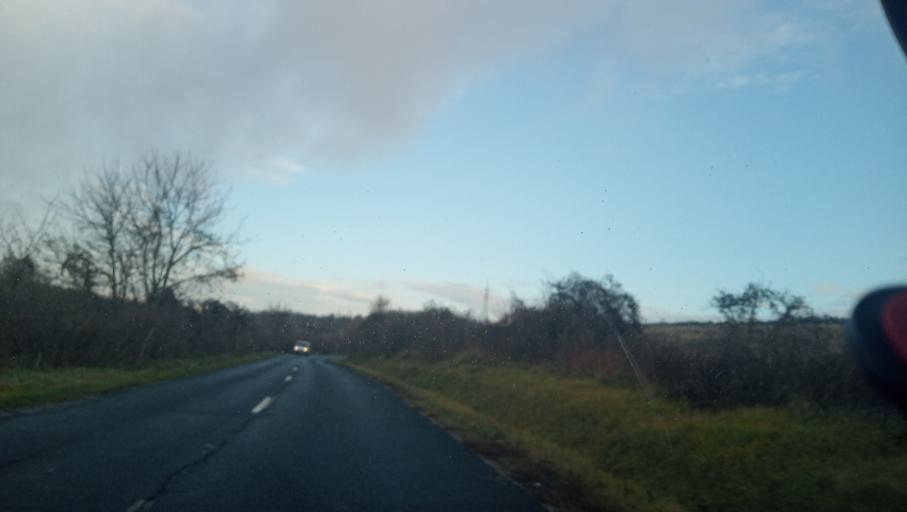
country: HU
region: Pest
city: Csobanka
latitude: 47.6340
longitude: 18.9550
